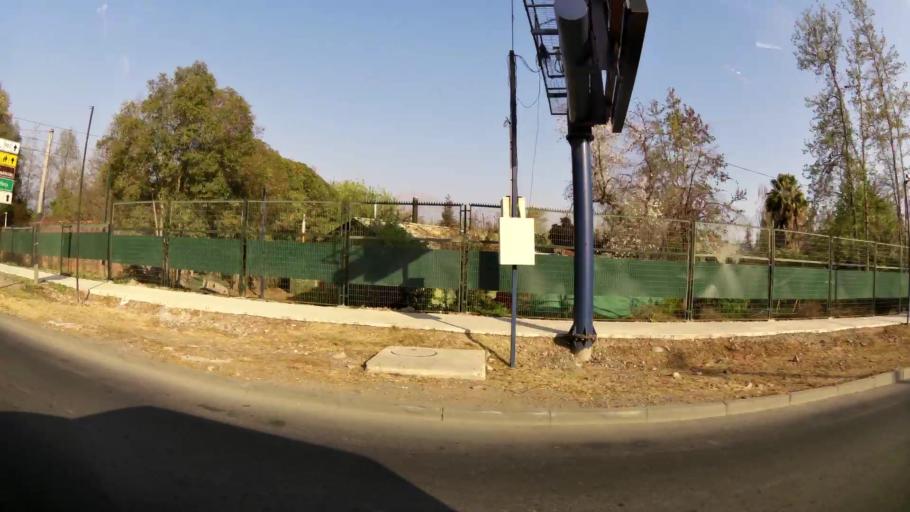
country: CL
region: Santiago Metropolitan
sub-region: Provincia de Santiago
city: Villa Presidente Frei, Nunoa, Santiago, Chile
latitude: -33.3540
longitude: -70.5255
